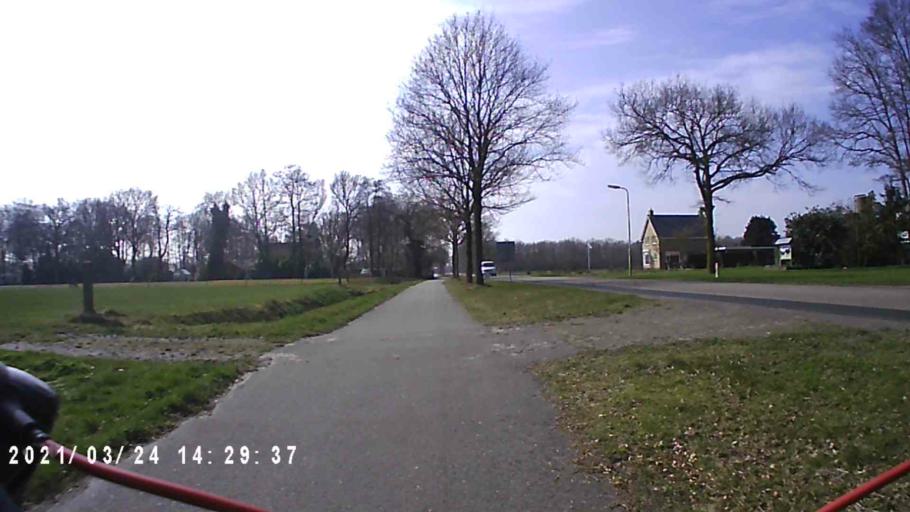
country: NL
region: Friesland
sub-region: Gemeente Heerenveen
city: Jubbega
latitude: 53.0361
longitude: 6.1619
